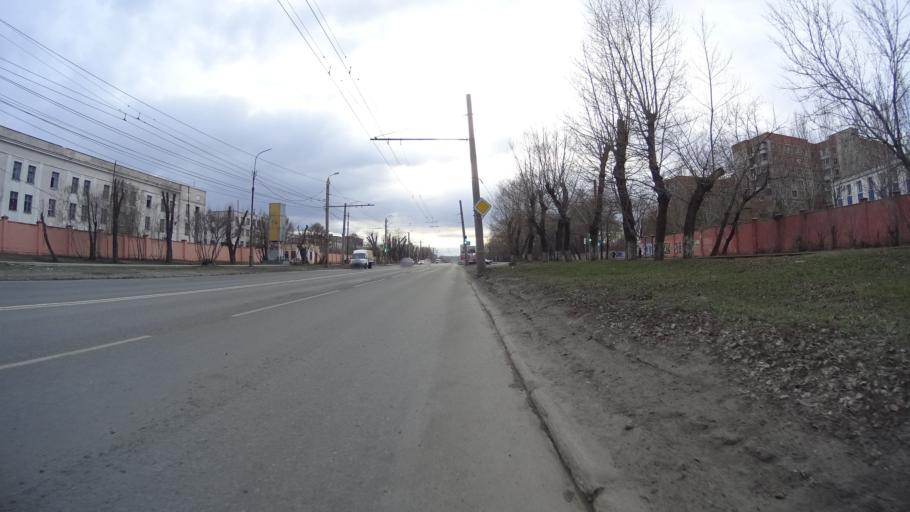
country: RU
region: Chelyabinsk
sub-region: Gorod Chelyabinsk
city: Chelyabinsk
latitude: 55.1596
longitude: 61.4597
